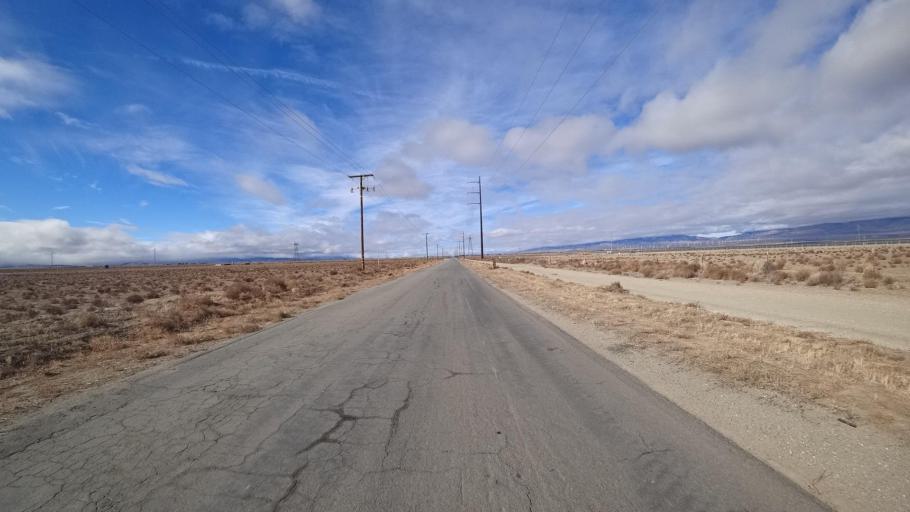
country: US
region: California
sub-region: Kern County
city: Rosamond
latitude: 34.8346
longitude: -118.3099
